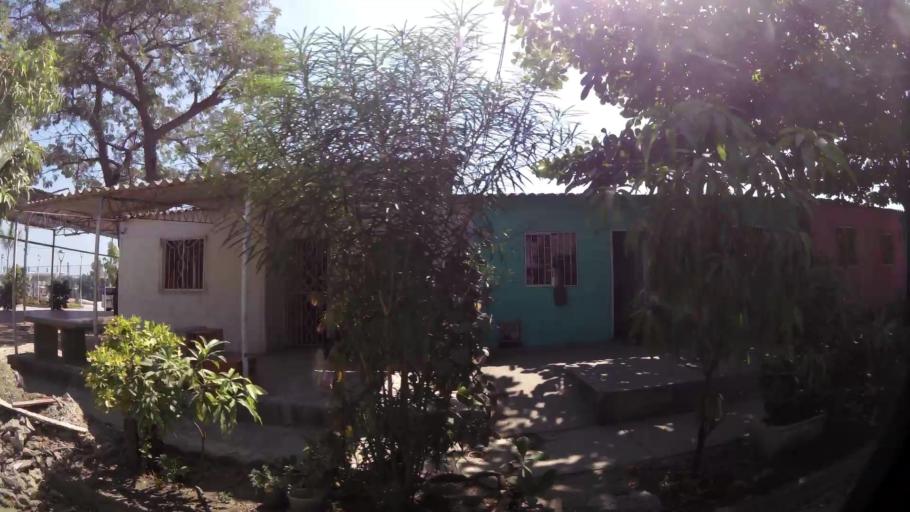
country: CO
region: Bolivar
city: Cartagena
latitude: 10.3919
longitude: -75.4533
